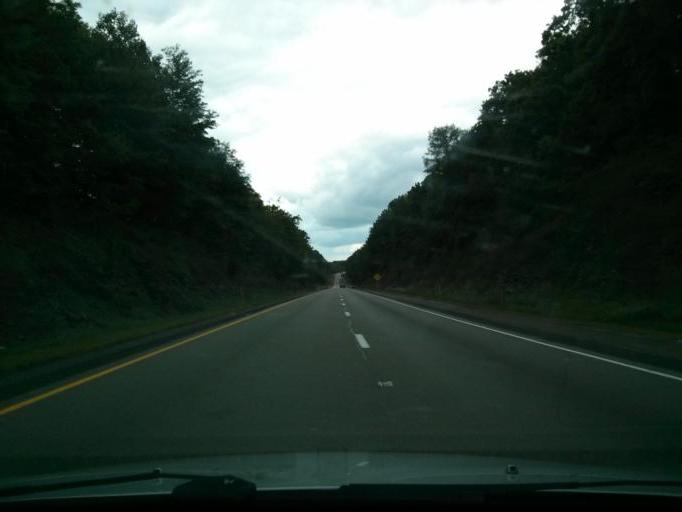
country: US
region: Pennsylvania
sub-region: Clarion County
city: Clarion
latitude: 41.1729
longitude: -79.2729
